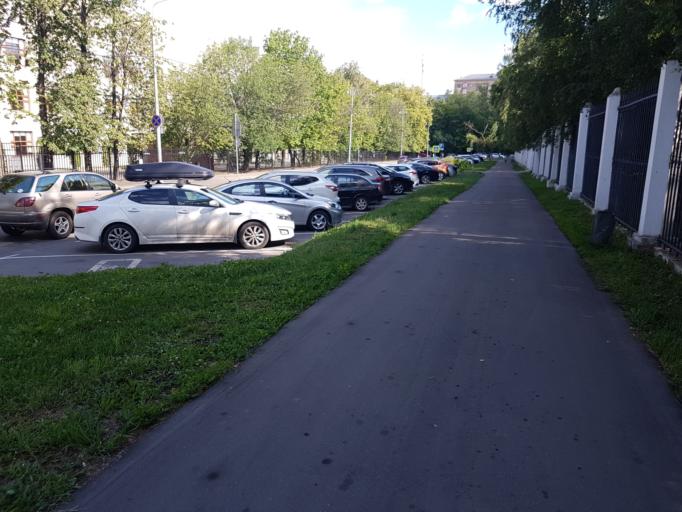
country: RU
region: Moskovskaya
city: Koptevo
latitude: 55.8208
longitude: 37.5037
